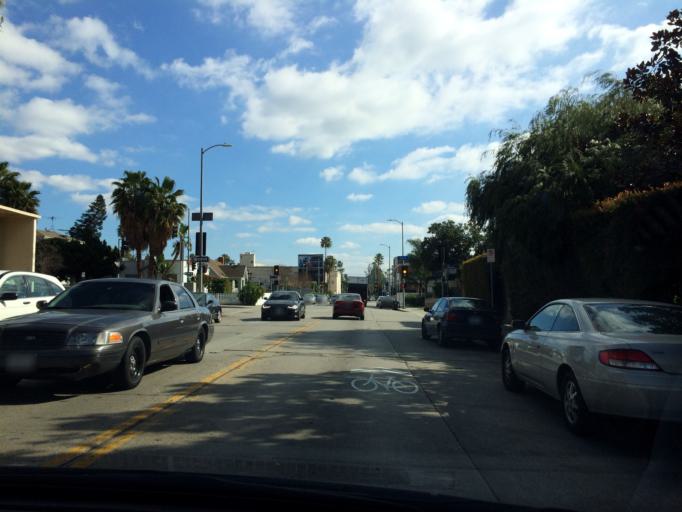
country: US
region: California
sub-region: Los Angeles County
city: Hollywood
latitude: 34.0943
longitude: -118.3305
